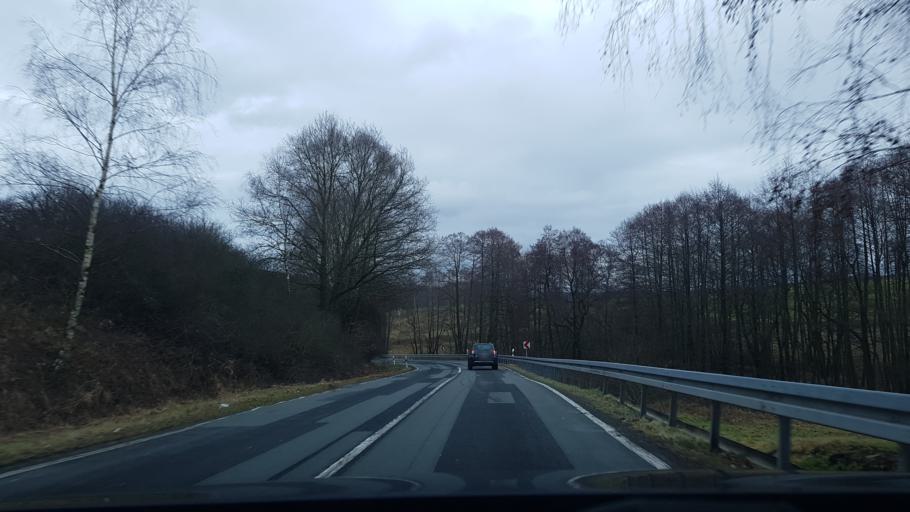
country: DE
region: Saxony
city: Dohma
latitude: 50.8326
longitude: 13.9674
